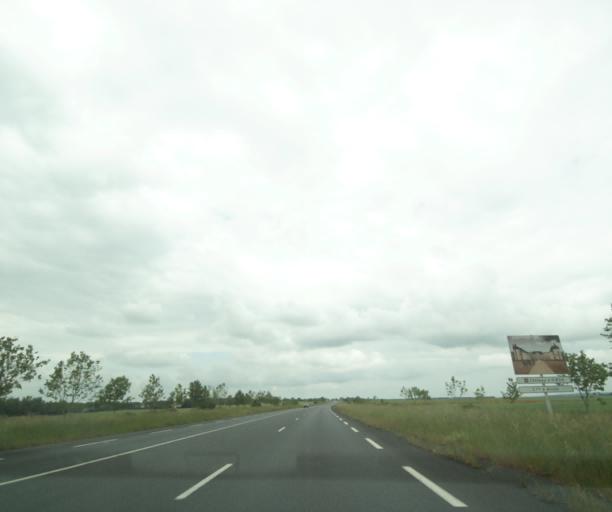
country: FR
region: Poitou-Charentes
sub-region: Departement des Deux-Sevres
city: Saint-Varent
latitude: 46.8936
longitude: -0.1933
